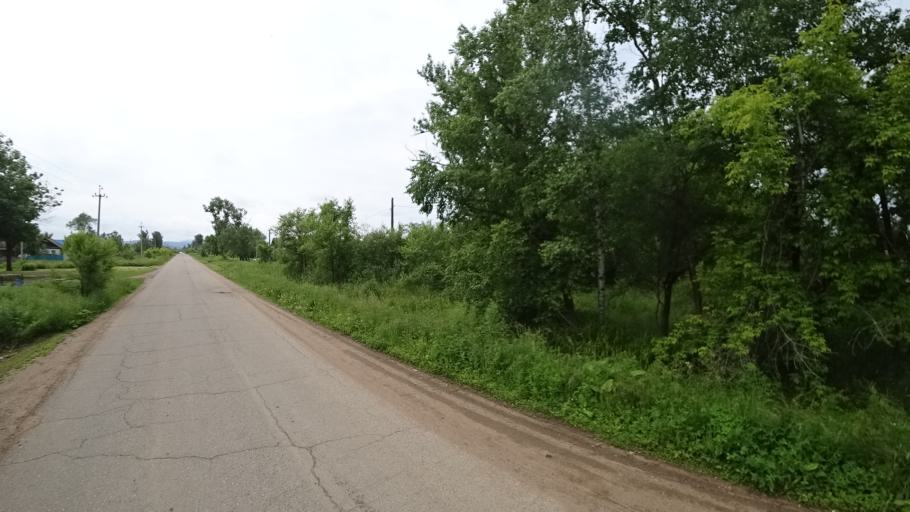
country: RU
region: Primorskiy
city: Novosysoyevka
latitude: 44.2430
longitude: 133.3675
